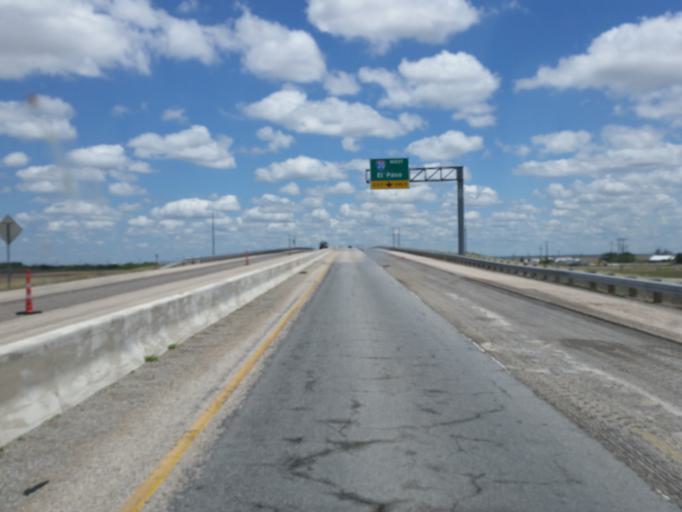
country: US
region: Texas
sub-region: Nolan County
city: Roscoe
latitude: 32.4516
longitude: -100.5240
